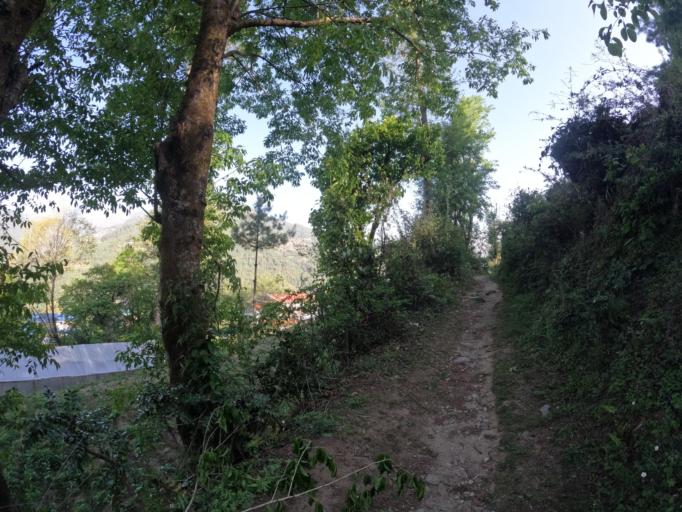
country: NP
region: Eastern Region
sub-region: Sagarmatha Zone
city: Namche Bazar
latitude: 27.4899
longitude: 86.5815
